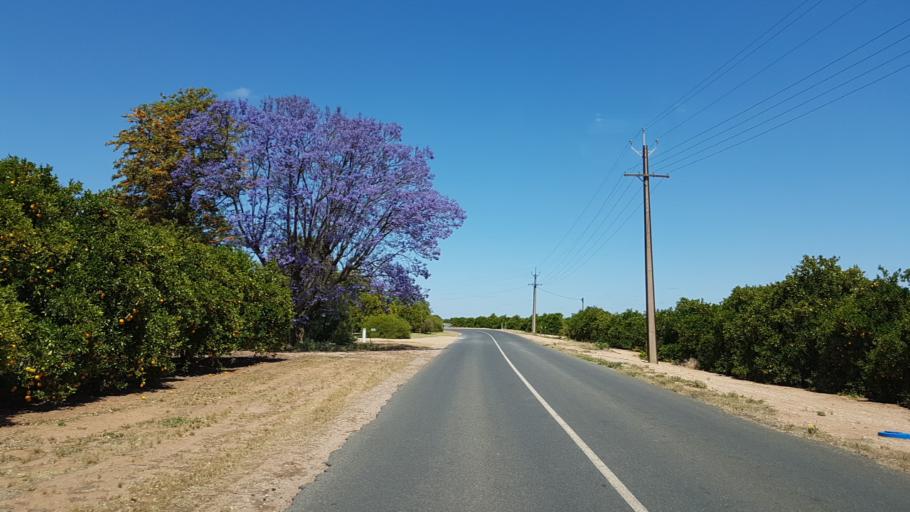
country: AU
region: South Australia
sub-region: Loxton Waikerie
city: Waikerie
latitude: -34.1756
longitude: 140.0288
